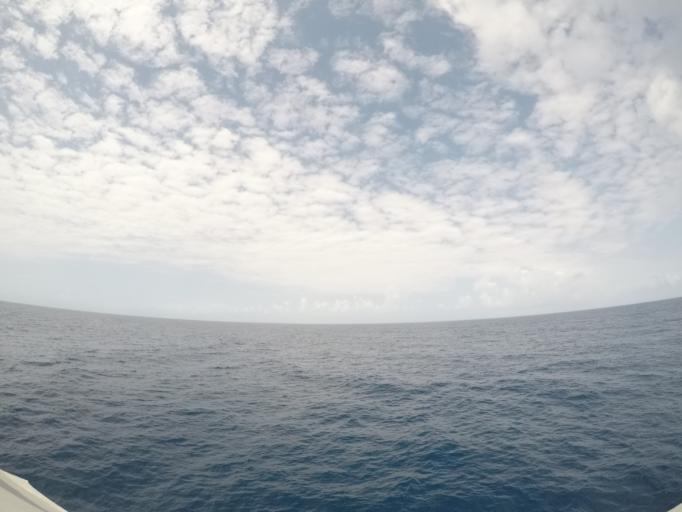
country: TZ
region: Zanzibar North
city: Nungwi
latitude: -5.5819
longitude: 39.3581
